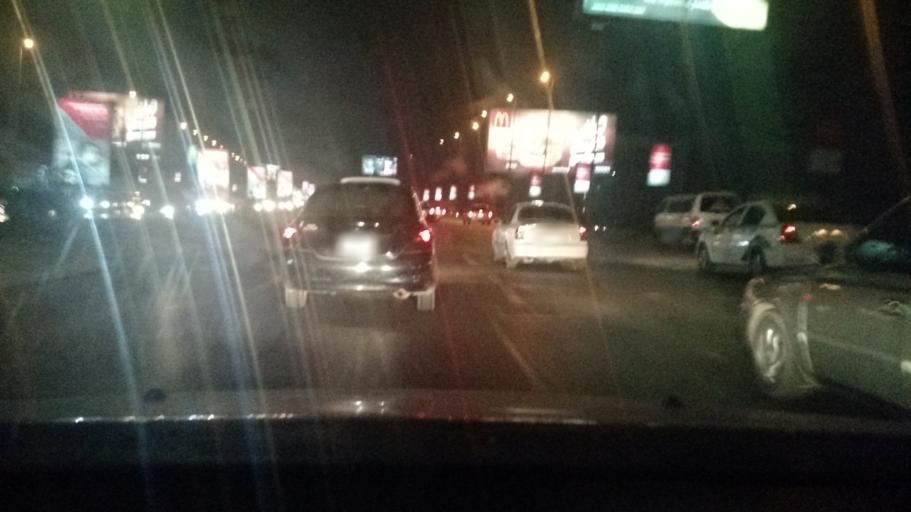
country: EG
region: Al Jizah
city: Al Jizah
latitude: 29.9867
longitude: 31.2172
